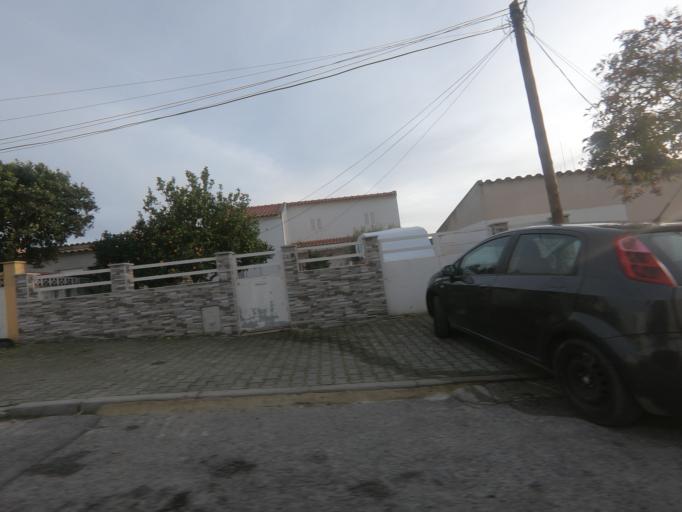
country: PT
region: Setubal
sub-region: Setubal
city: Setubal
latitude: 38.5345
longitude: -8.8786
